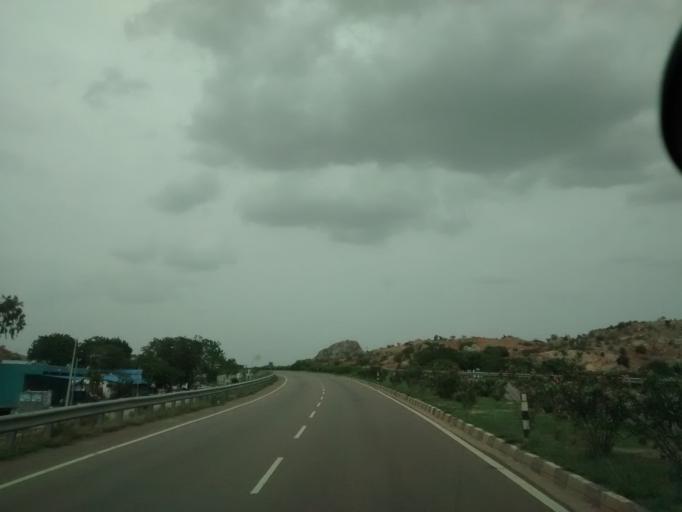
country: IN
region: Andhra Pradesh
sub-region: Kurnool
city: Ramapuram
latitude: 15.1596
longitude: 77.6721
